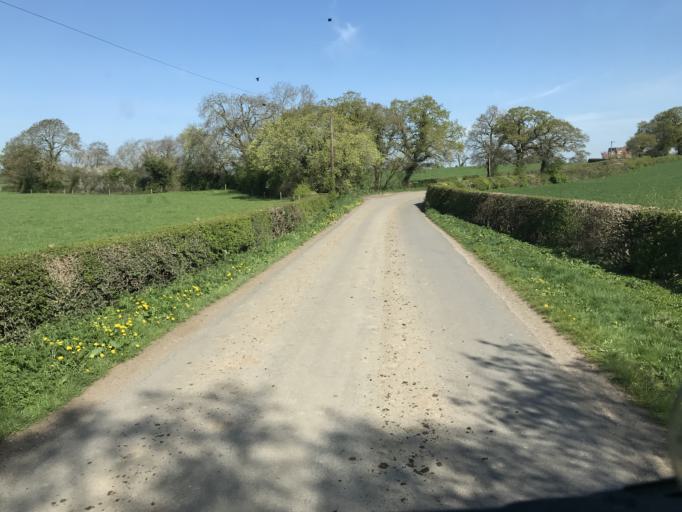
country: GB
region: England
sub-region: Cheshire East
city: Middlewich
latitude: 53.1890
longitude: -2.4679
